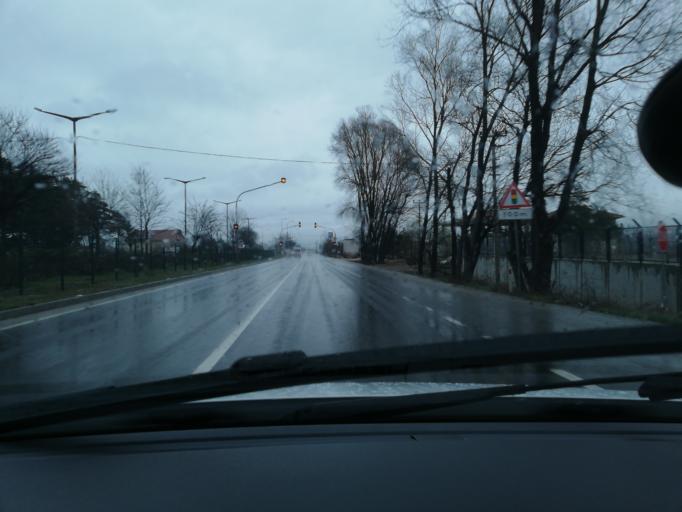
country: TR
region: Bolu
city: Bolu
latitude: 40.7368
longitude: 31.6518
